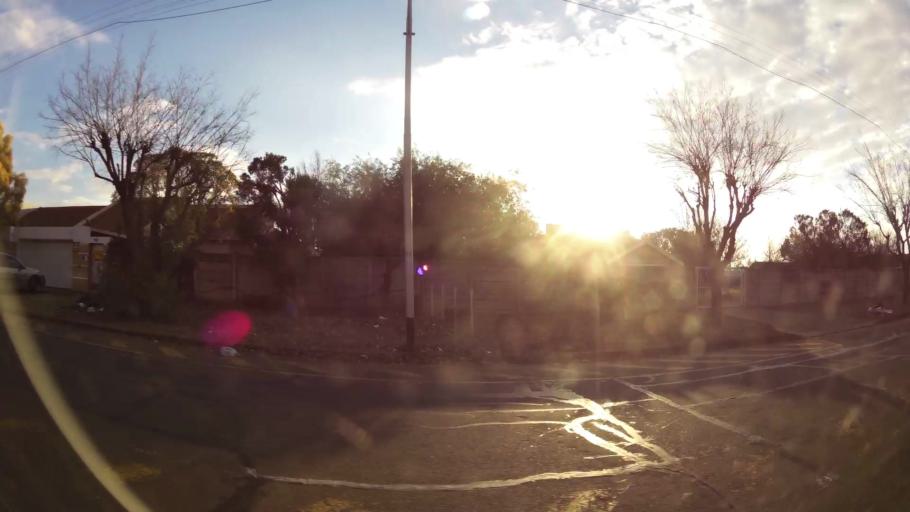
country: ZA
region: Orange Free State
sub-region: Mangaung Metropolitan Municipality
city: Bloemfontein
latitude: -29.1388
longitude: 26.1931
